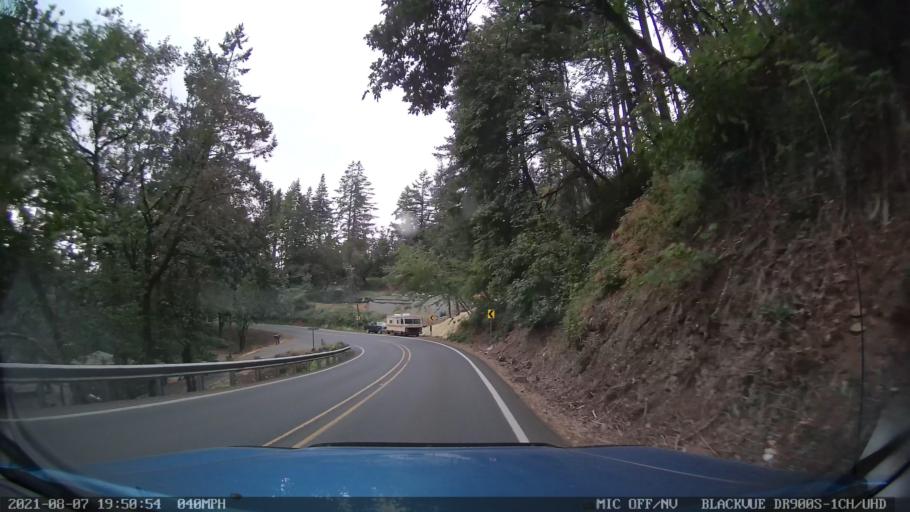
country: US
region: Oregon
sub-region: Marion County
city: Silverton
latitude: 44.9858
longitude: -122.7439
